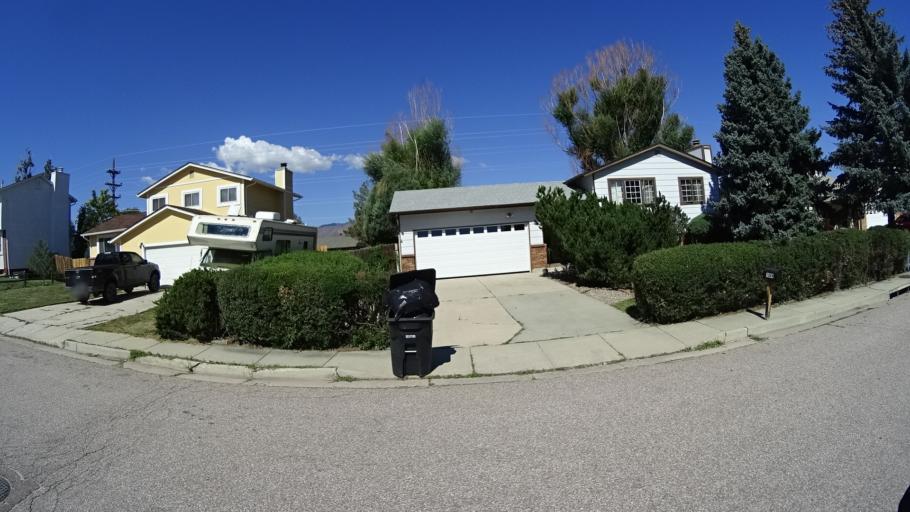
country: US
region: Colorado
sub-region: El Paso County
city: Air Force Academy
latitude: 38.9420
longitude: -104.7932
